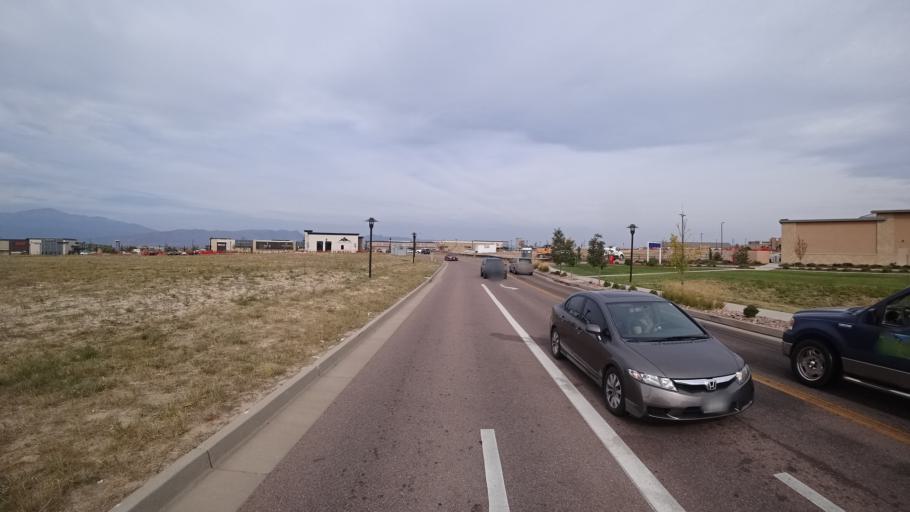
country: US
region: Colorado
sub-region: El Paso County
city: Cimarron Hills
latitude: 38.9244
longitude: -104.7159
